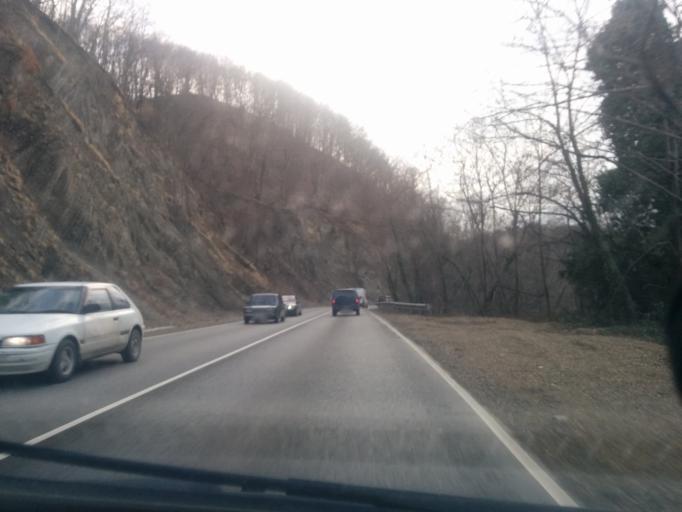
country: RU
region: Krasnodarskiy
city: Agoy
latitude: 44.1345
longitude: 39.0508
